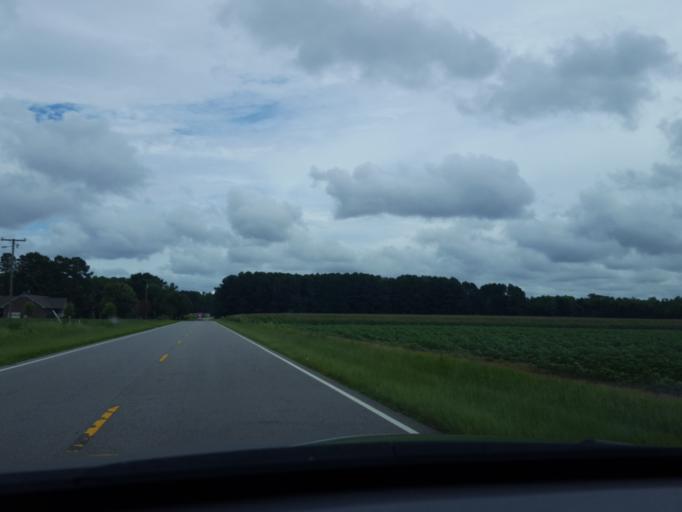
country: US
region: North Carolina
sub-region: Martin County
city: Williamston
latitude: 35.7073
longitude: -76.9866
